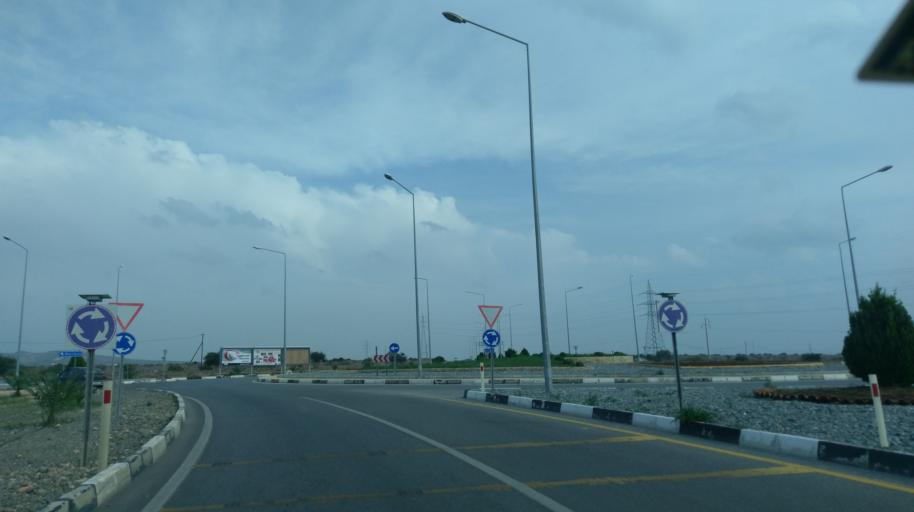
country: CY
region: Lefkosia
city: Astromeritis
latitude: 35.1961
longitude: 33.0638
